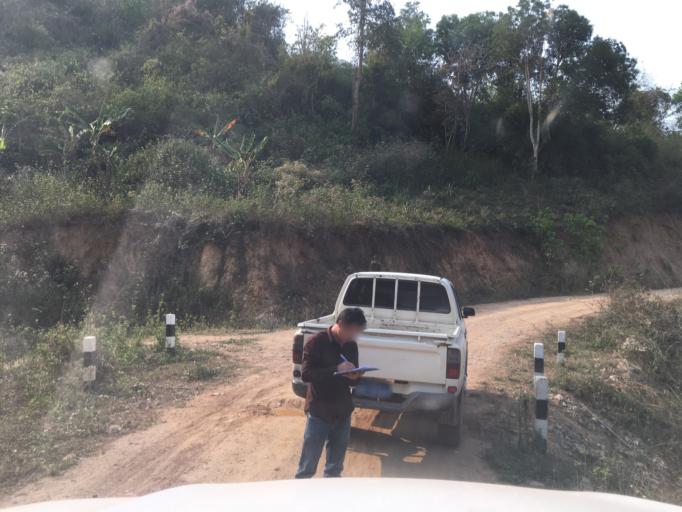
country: LA
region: Xiangkhoang
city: Phonsavan
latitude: 19.8227
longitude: 102.9931
